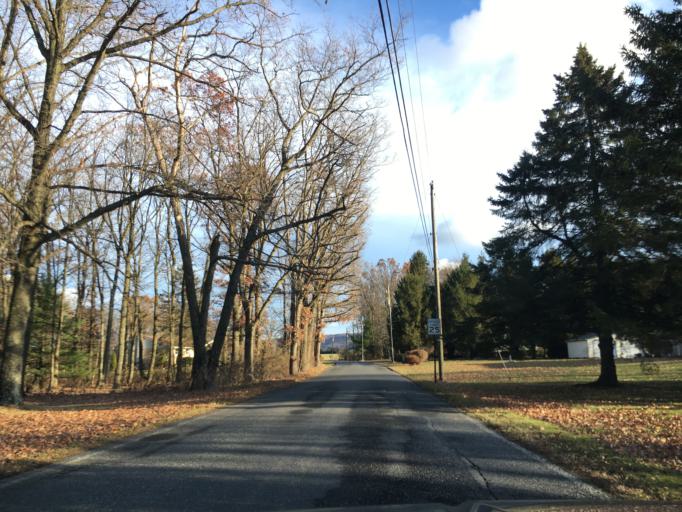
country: US
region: Pennsylvania
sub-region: Carbon County
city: Lehighton
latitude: 40.8015
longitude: -75.7294
